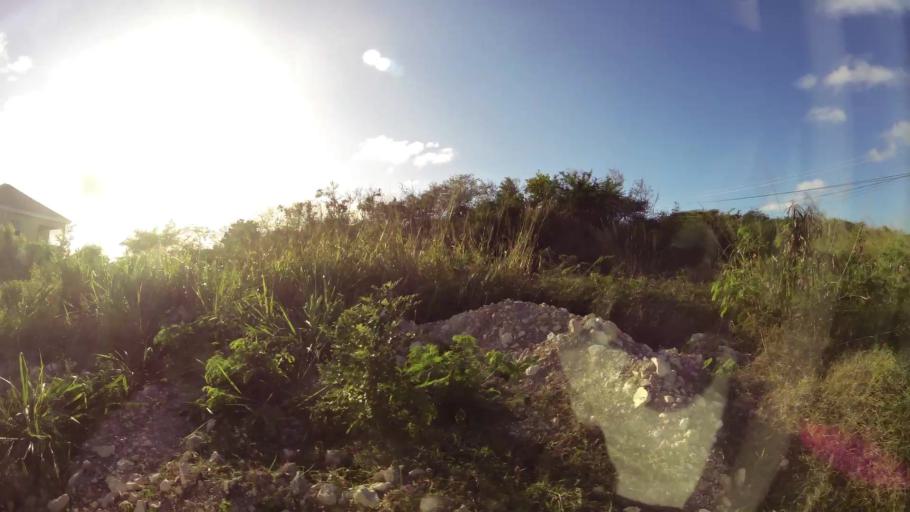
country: AG
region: Saint George
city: Piggotts
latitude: 17.1288
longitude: -61.7933
